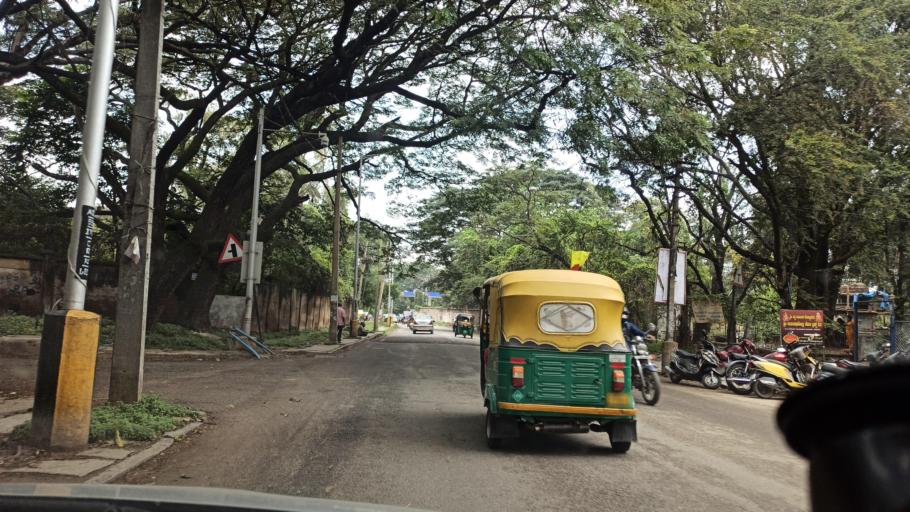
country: IN
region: Karnataka
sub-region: Bangalore Urban
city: Bangalore
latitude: 13.0089
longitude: 77.6827
